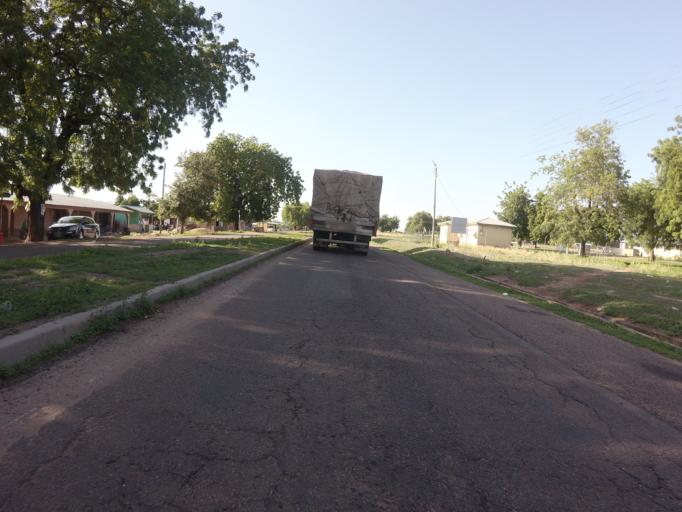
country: GH
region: Upper East
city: Navrongo
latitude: 10.9002
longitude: -1.0923
